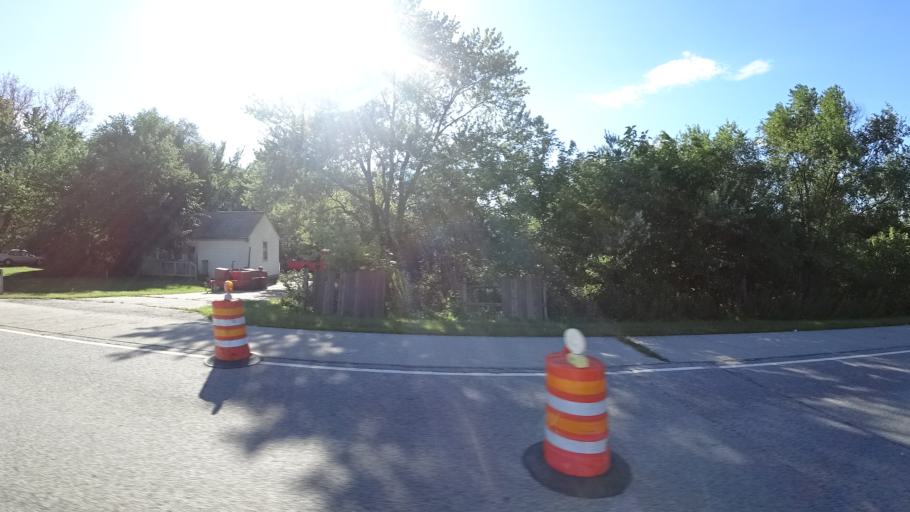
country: US
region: Illinois
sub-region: Cook County
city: Oak Forest
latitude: 41.5864
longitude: -87.7359
